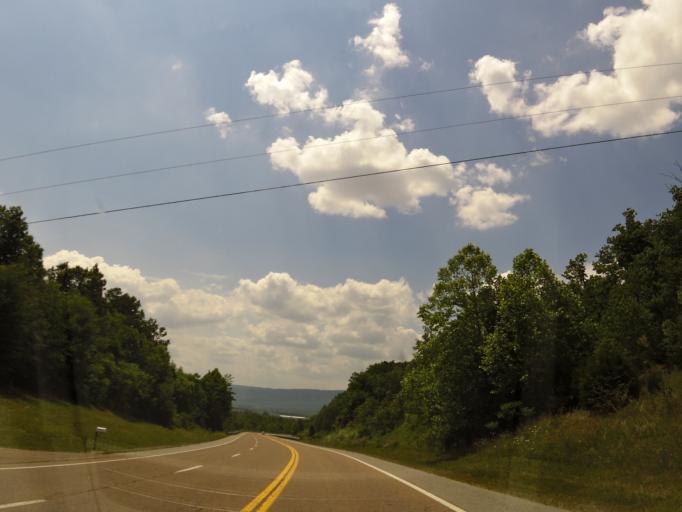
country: US
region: Tennessee
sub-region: Bledsoe County
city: Pikeville
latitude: 35.5806
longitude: -85.1617
